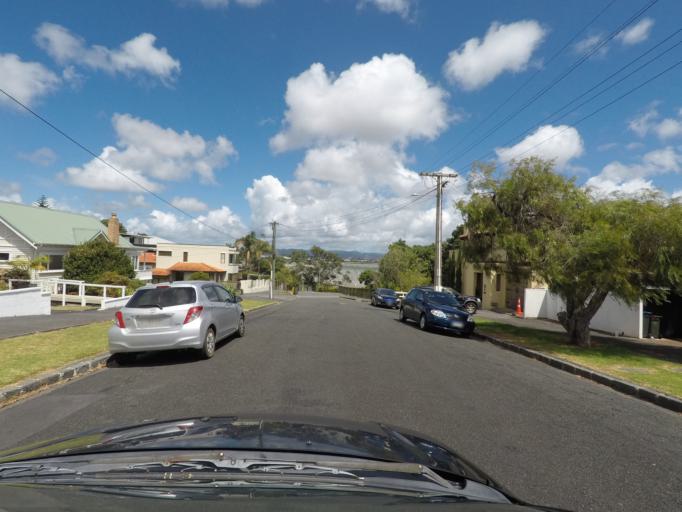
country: NZ
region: Auckland
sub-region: Auckland
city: Rosebank
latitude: -36.8634
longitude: 174.6990
